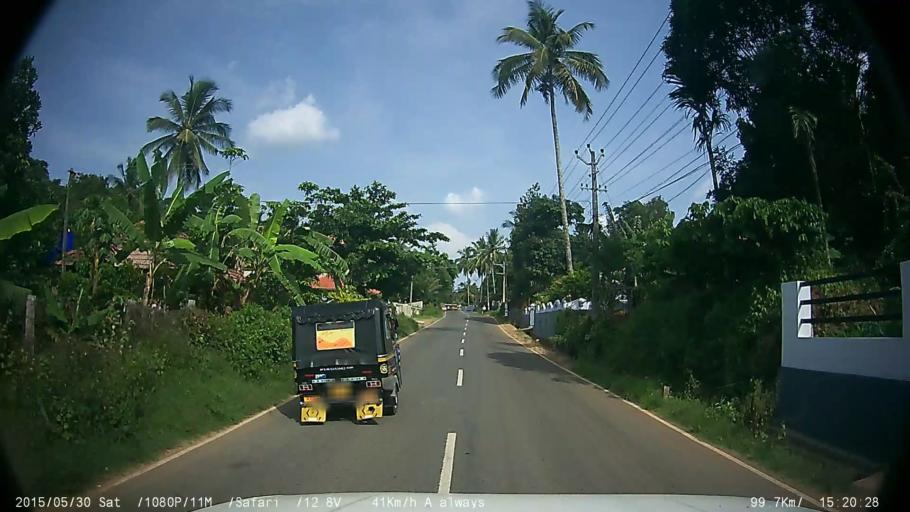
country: IN
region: Kerala
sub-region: Wayanad
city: Panamaram
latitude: 11.7540
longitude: 76.0651
